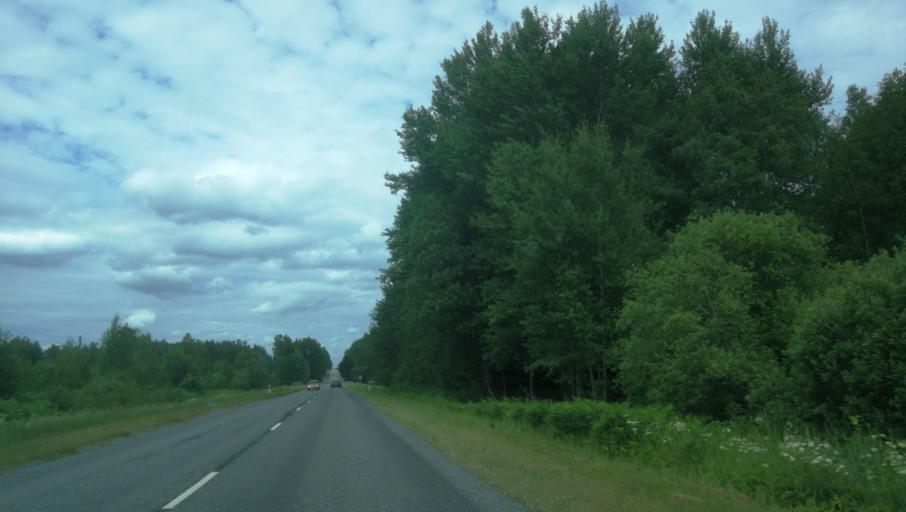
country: LV
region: Naukseni
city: Naukseni
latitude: 57.7831
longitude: 25.4266
